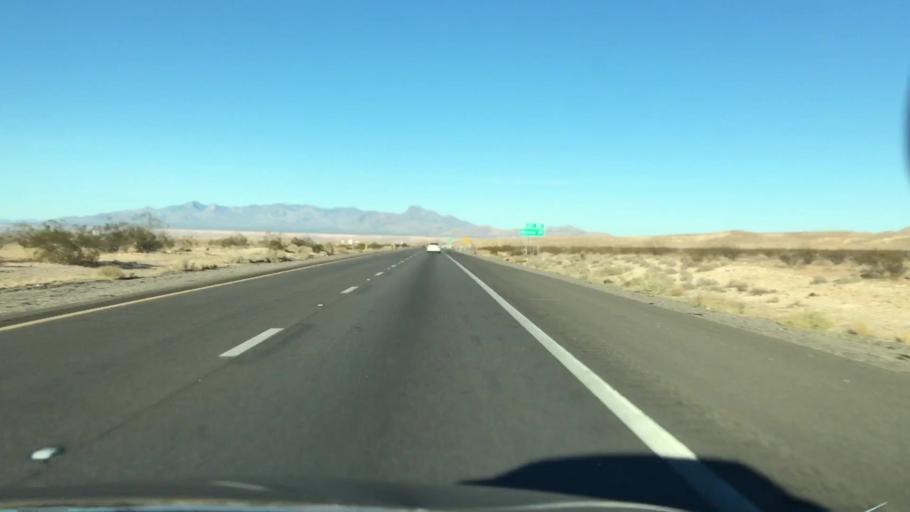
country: US
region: Nevada
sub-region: Clark County
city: Moapa Town
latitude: 36.5855
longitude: -114.6512
